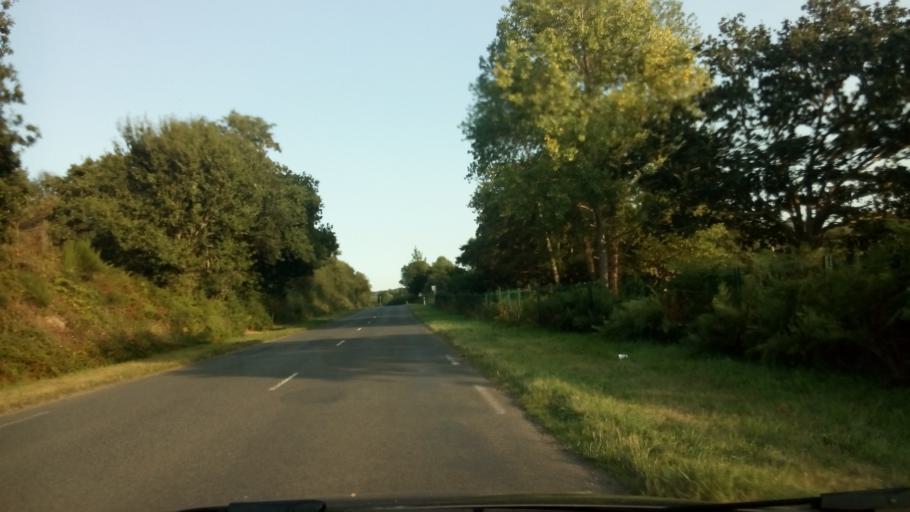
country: FR
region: Brittany
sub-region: Departement des Cotes-d'Armor
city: Trebeurden
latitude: 48.7874
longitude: -3.5433
